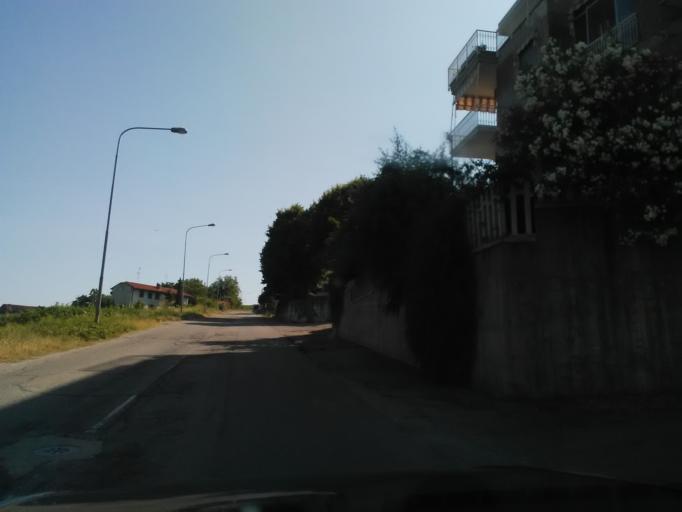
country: IT
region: Piedmont
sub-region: Provincia di Alessandria
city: Casale Monferrato
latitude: 45.1287
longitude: 8.4416
